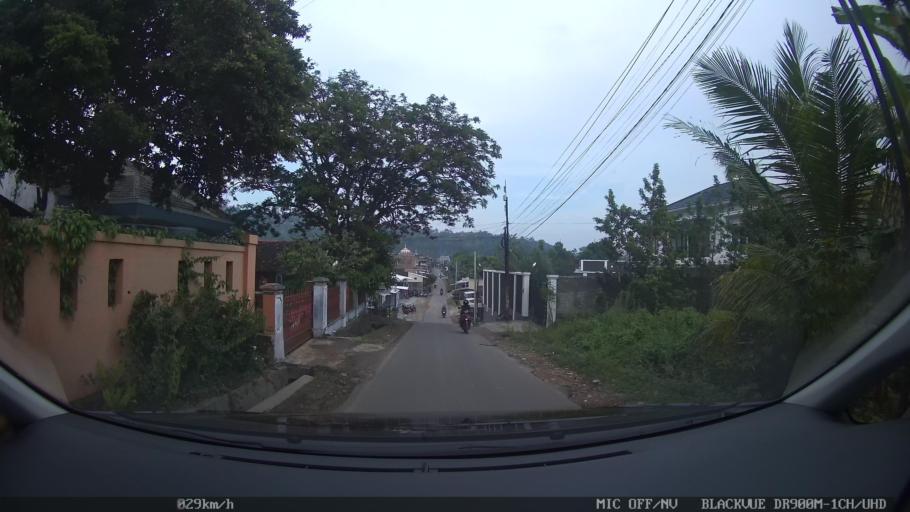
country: ID
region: Lampung
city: Kedaton
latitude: -5.4008
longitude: 105.2317
